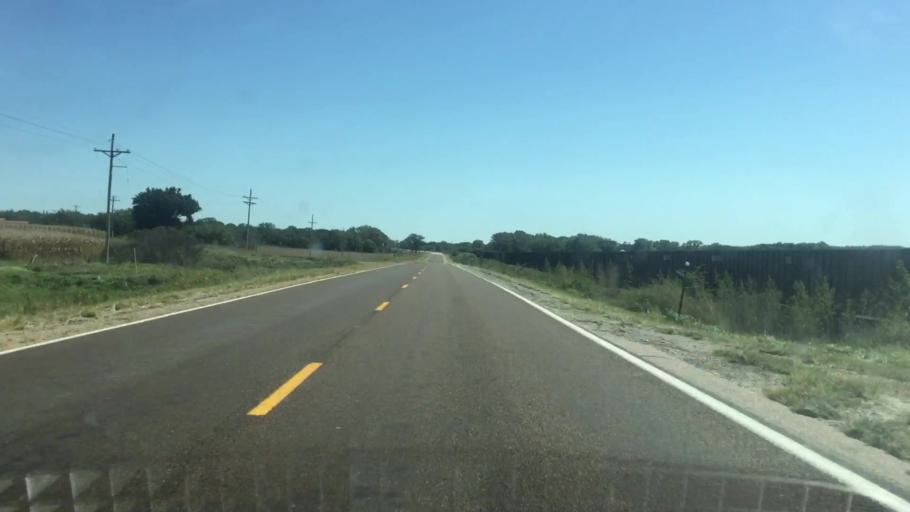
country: US
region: Nebraska
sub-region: Jefferson County
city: Fairbury
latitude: 40.0851
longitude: -97.1145
